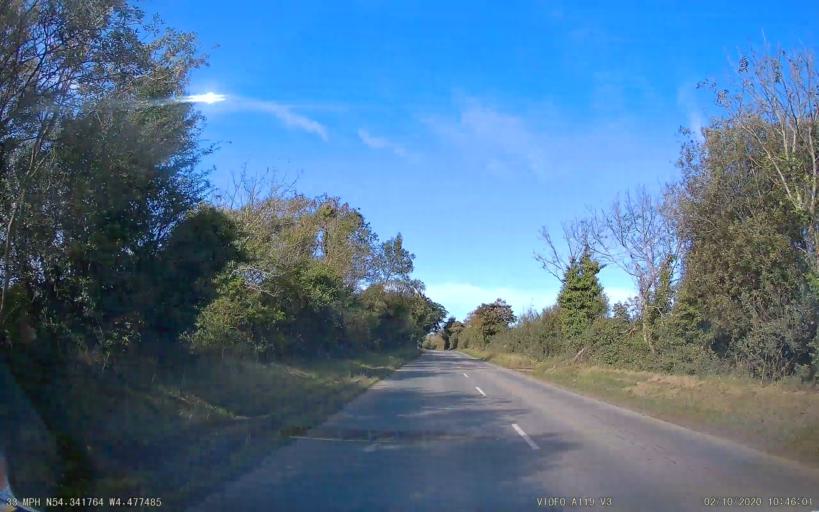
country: IM
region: Ramsey
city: Ramsey
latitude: 54.3418
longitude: -4.4775
